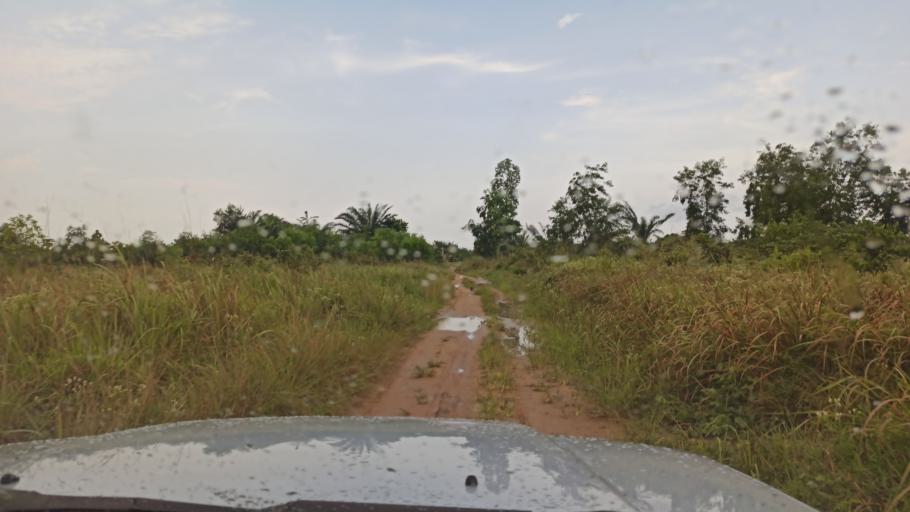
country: BJ
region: Queme
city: Porto-Novo
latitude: 6.4539
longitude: 2.6678
